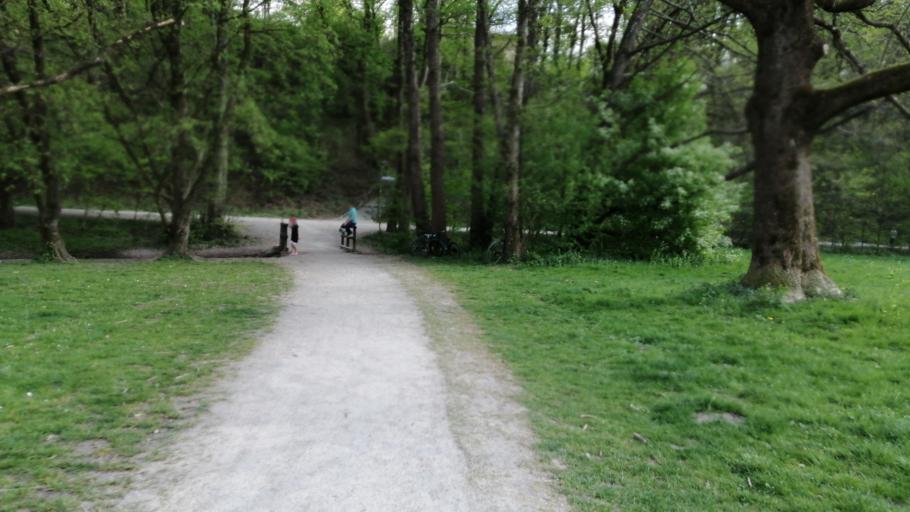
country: DE
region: Bavaria
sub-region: Upper Bavaria
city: Bogenhausen
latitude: 48.1632
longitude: 11.6191
